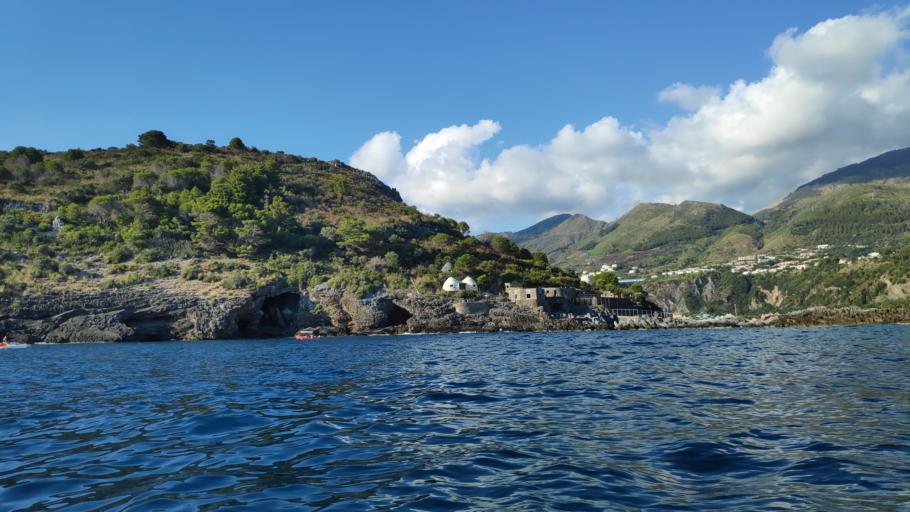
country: IT
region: Calabria
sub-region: Provincia di Cosenza
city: Praia a Mare
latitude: 39.8710
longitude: 15.7780
